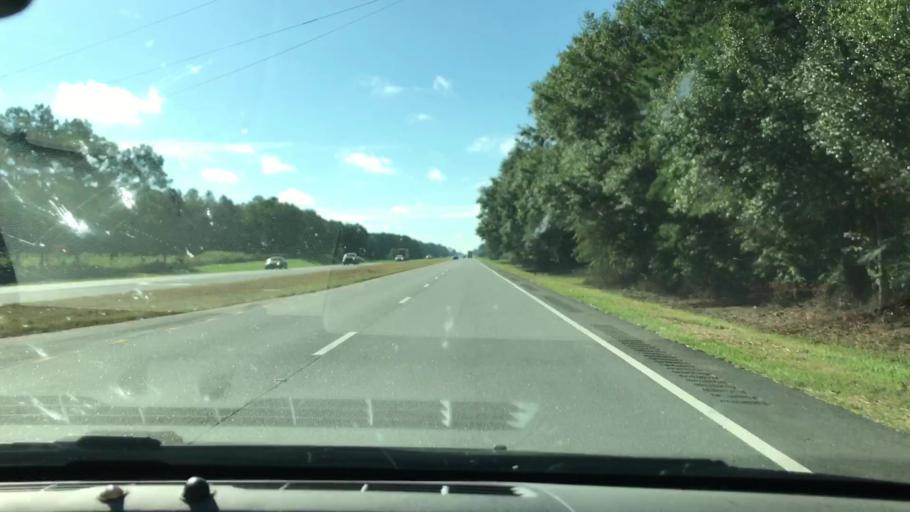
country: US
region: Georgia
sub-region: Lee County
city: Leesburg
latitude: 31.6791
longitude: -84.2984
